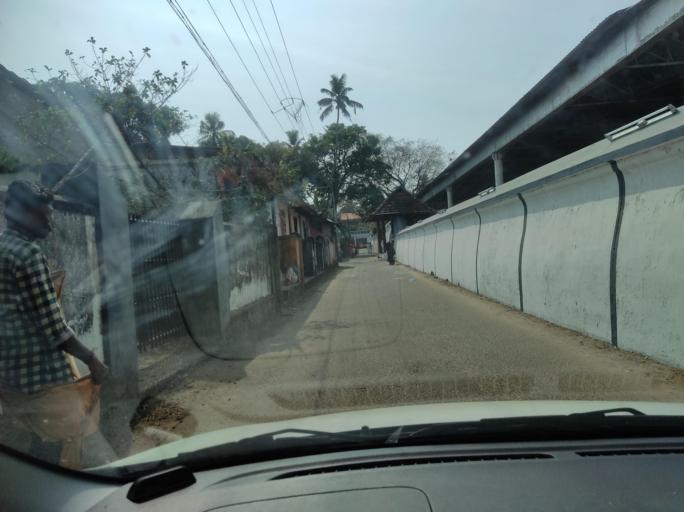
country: IN
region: Kerala
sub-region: Kottayam
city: Kottayam
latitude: 9.6731
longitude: 76.5616
